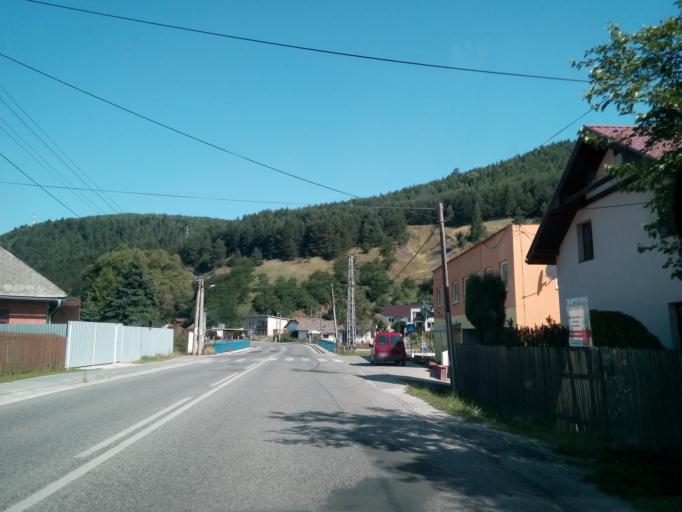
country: SK
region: Kosicky
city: Krompachy
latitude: 48.9264
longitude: 20.8569
